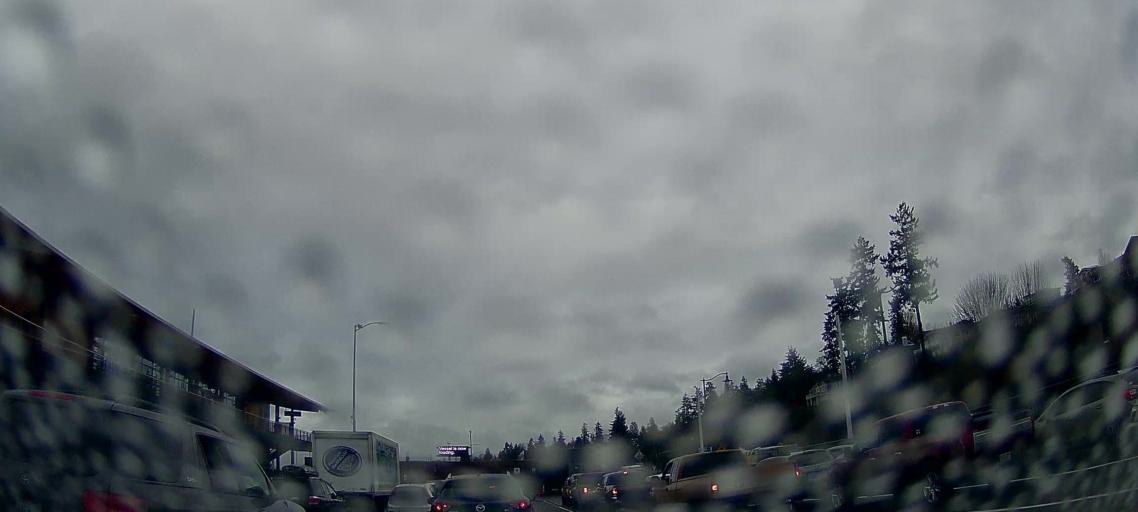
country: US
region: Washington
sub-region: Snohomish County
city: Mukilteo
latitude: 47.9498
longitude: -122.2976
